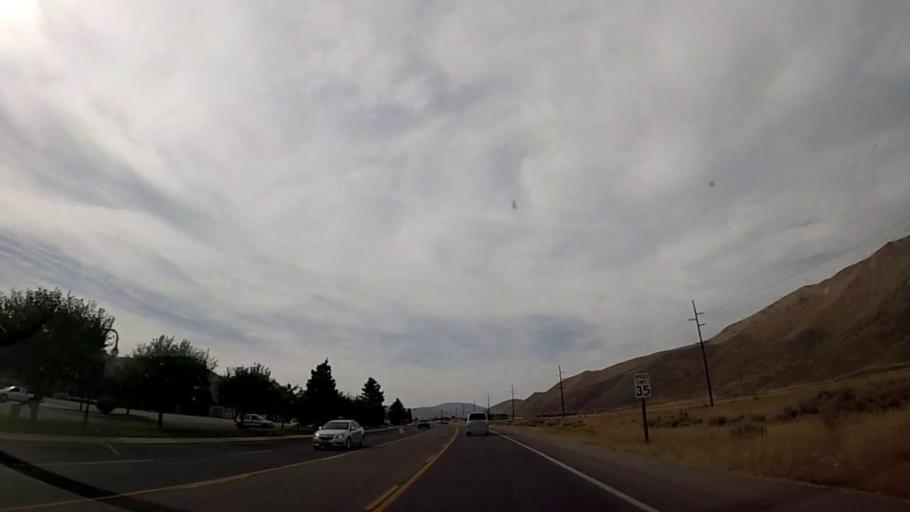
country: US
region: Idaho
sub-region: Blaine County
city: Bellevue
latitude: 43.4744
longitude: -114.2655
